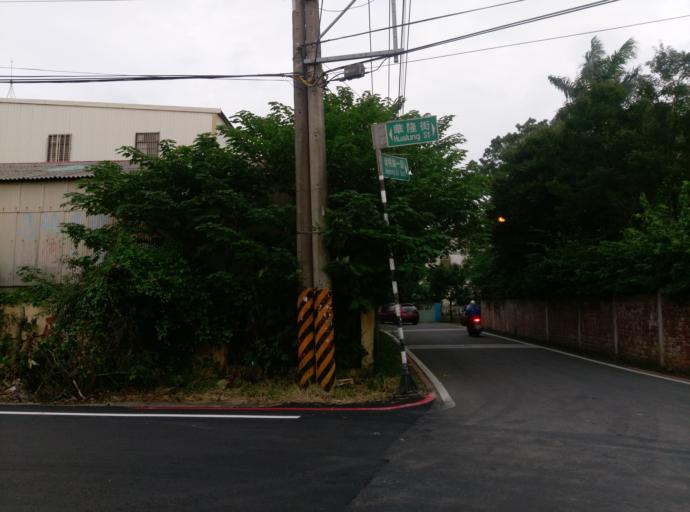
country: TW
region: Taiwan
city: Daxi
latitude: 24.9169
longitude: 121.2381
